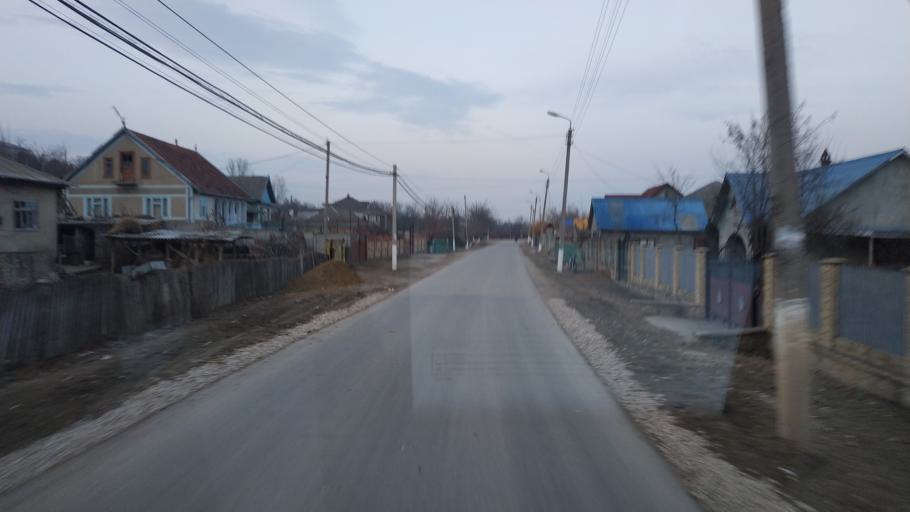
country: RO
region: Vaslui
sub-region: Comuna Stanilesti
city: Stanilesti
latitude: 46.6498
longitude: 28.3035
